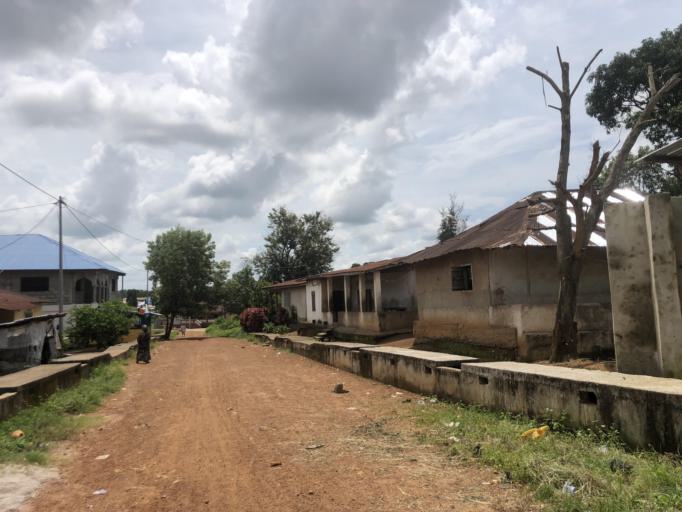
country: SL
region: Northern Province
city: Makeni
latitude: 8.8798
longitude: -12.0488
